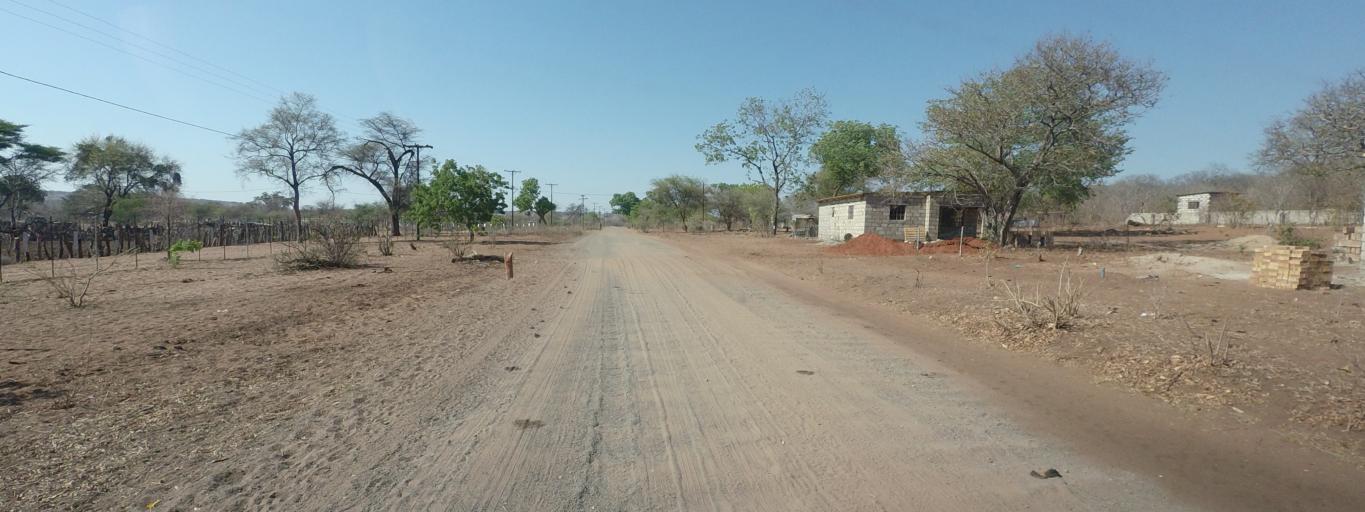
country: BW
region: North West
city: Kasane
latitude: -17.8935
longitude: 25.2291
